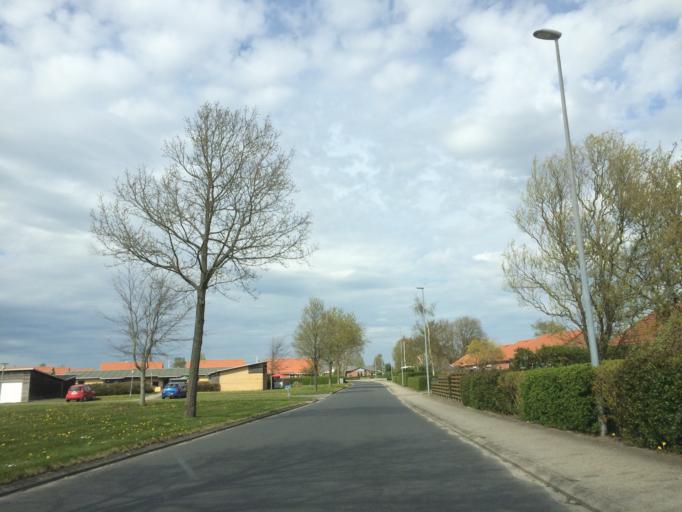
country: DK
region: Central Jutland
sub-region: Viborg Kommune
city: Bjerringbro
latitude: 56.2632
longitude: 9.7284
